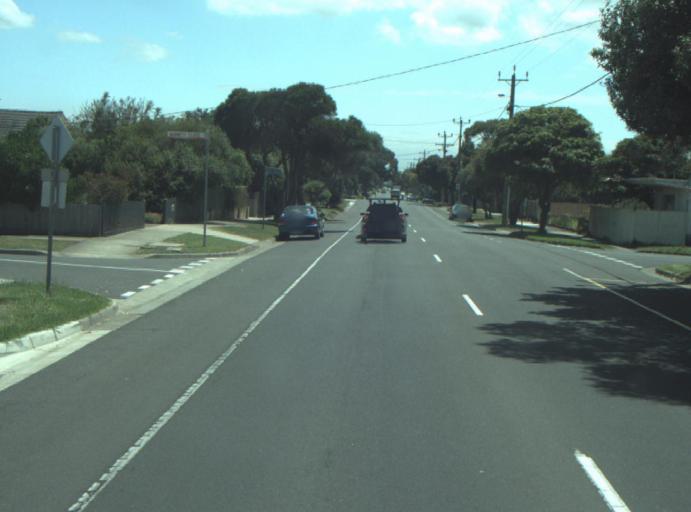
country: AU
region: Victoria
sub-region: Greater Geelong
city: Leopold
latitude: -38.2807
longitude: 144.4874
